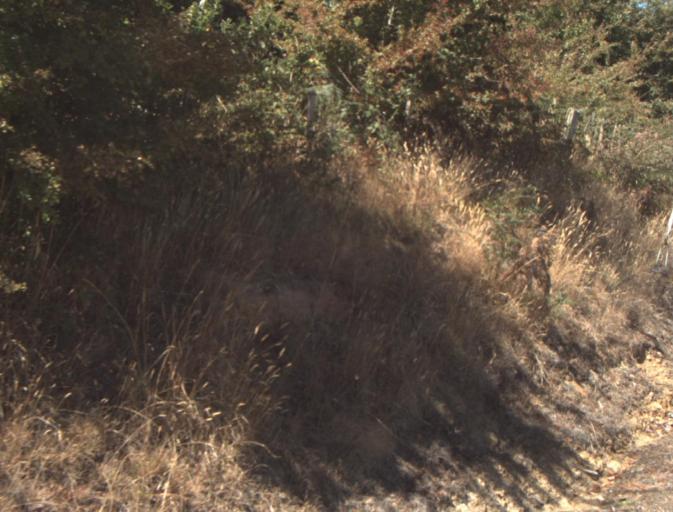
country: AU
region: Tasmania
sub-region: Launceston
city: Newstead
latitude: -41.3501
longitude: 147.3035
